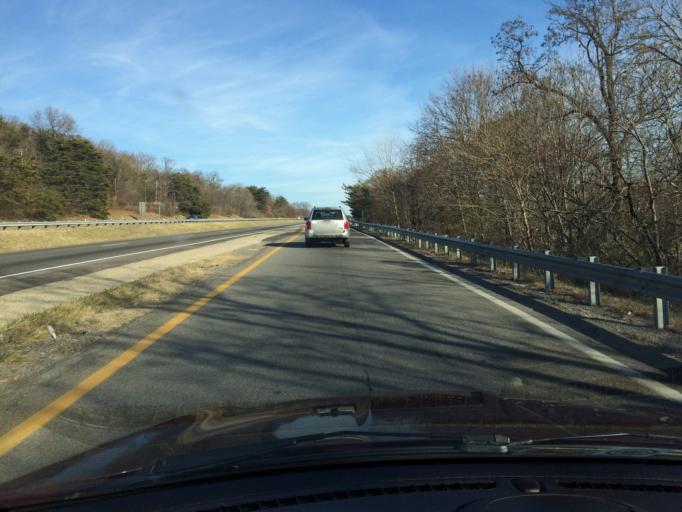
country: US
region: Virginia
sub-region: City of Salem
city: Salem
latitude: 37.2949
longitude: -80.0934
